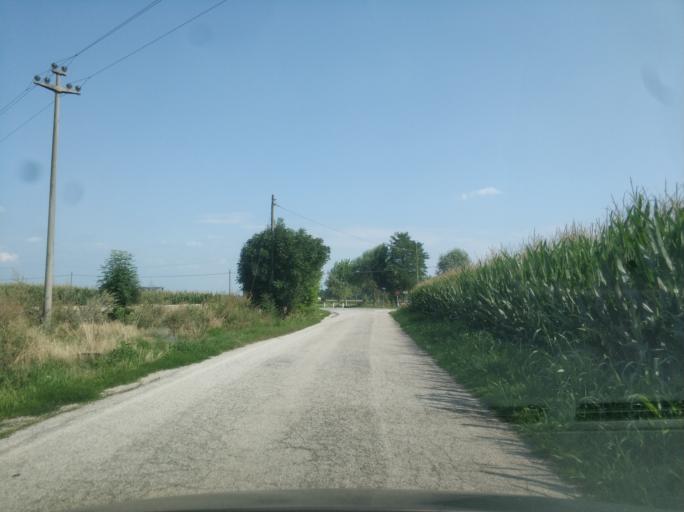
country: IT
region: Piedmont
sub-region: Provincia di Cuneo
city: Roata Rossi
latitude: 44.4528
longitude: 7.4816
